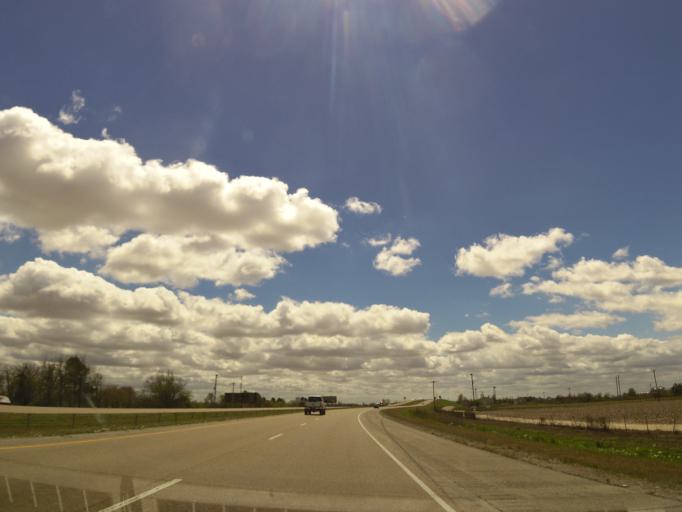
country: US
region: Arkansas
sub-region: Craighead County
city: Bay
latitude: 35.7653
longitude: -90.5768
